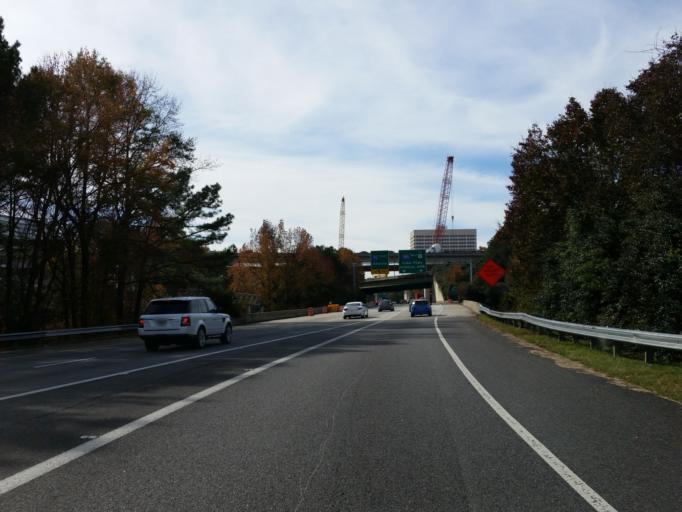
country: US
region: Georgia
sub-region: Cobb County
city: Vinings
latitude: 33.8916
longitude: -84.4605
